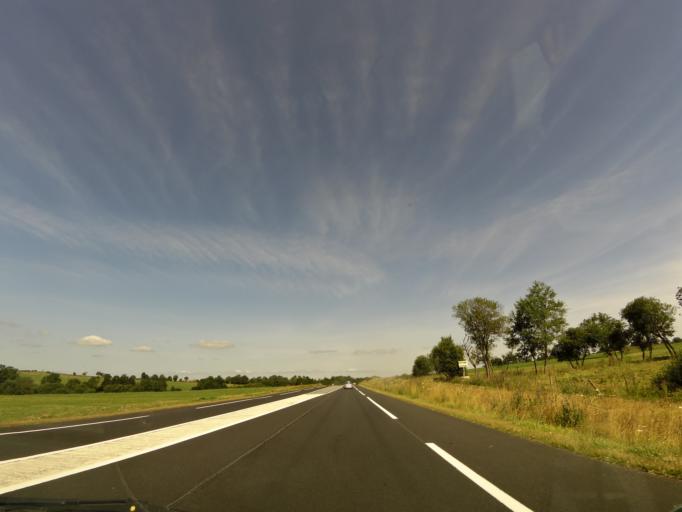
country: FR
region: Auvergne
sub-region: Departement du Puy-de-Dome
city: Aydat
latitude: 45.6937
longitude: 2.9206
